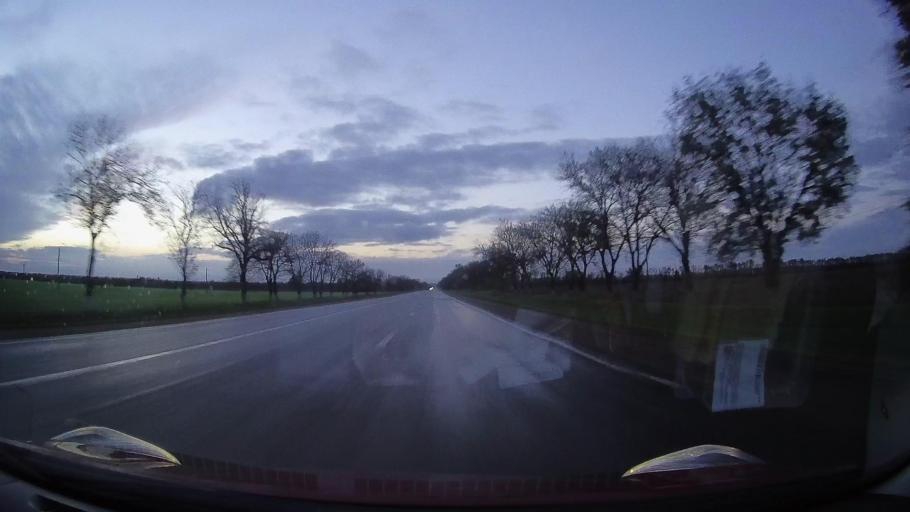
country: RU
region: Krasnodarskiy
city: Zavetnyy
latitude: 44.8946
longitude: 41.1980
